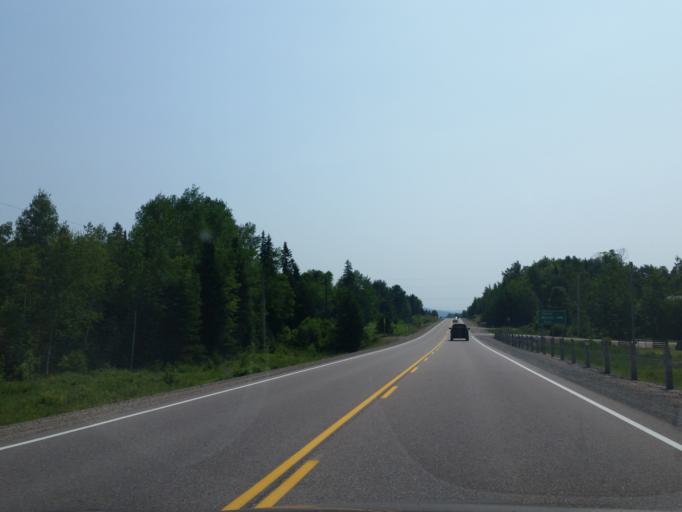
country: CA
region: Ontario
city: Mattawa
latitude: 46.3068
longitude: -78.6359
